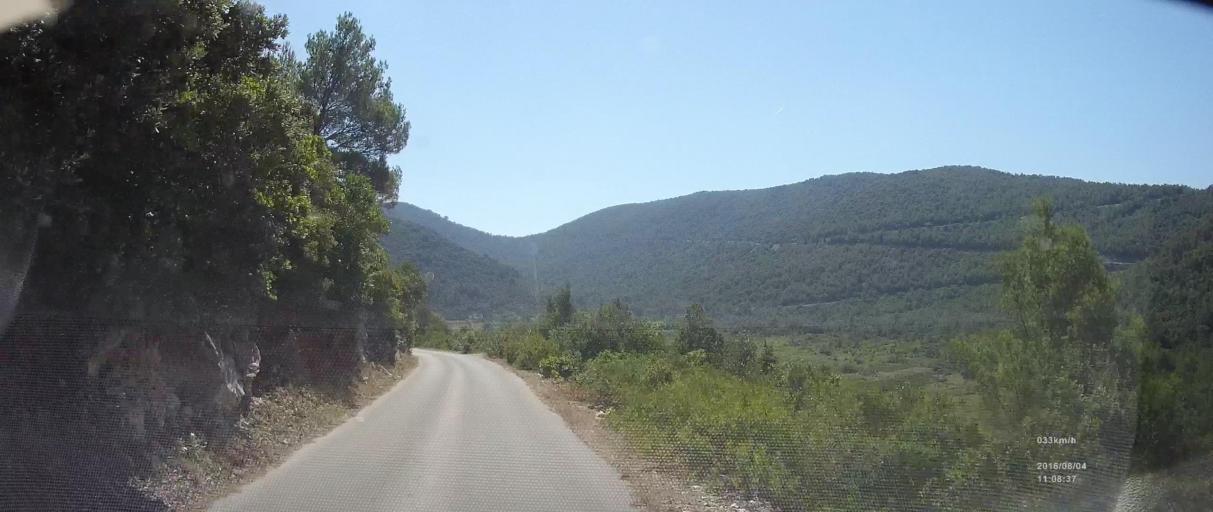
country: HR
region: Dubrovacko-Neretvanska
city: Blato
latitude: 42.7649
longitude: 17.4709
